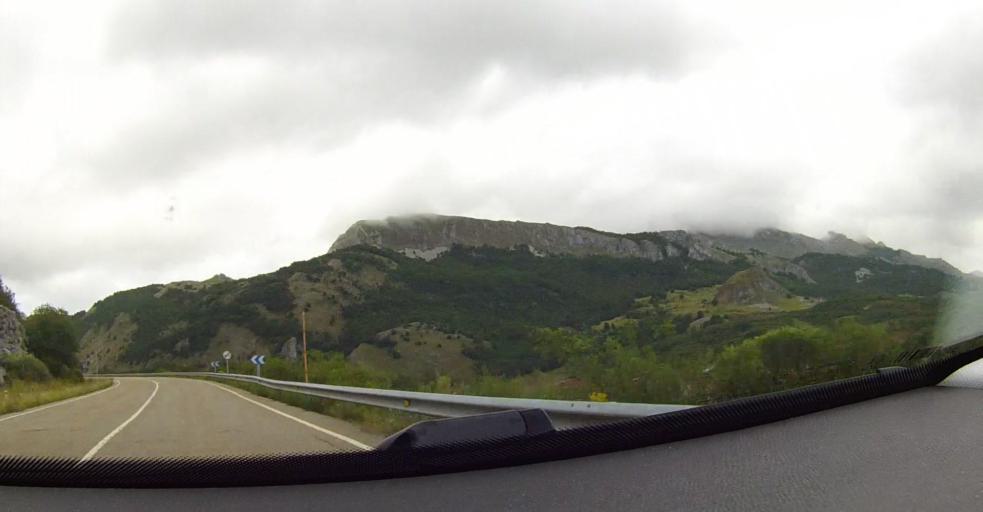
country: ES
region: Castille and Leon
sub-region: Provincia de Leon
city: Buron
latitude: 43.0198
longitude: -5.0359
